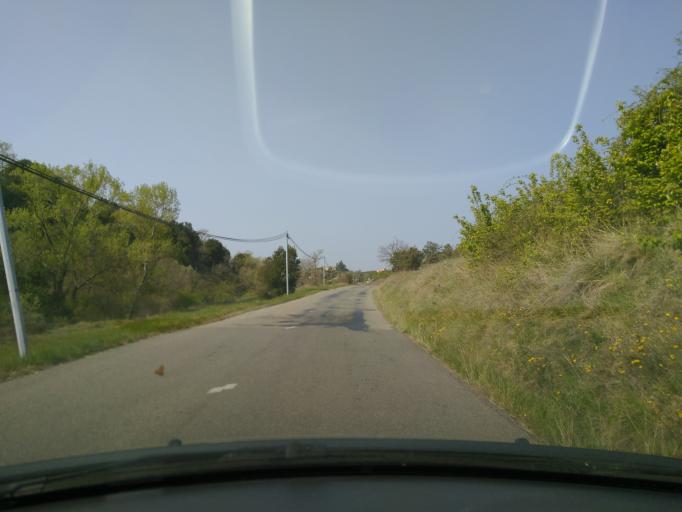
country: FR
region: Rhone-Alpes
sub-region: Departement de l'Ardeche
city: Ruoms
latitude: 44.4602
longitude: 4.4095
